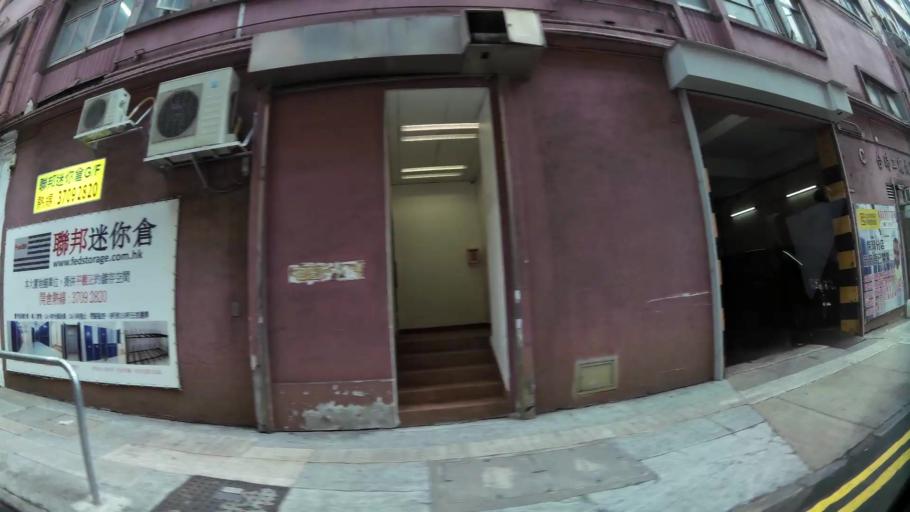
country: HK
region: Wanchai
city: Wan Chai
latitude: 22.2656
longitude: 114.2355
